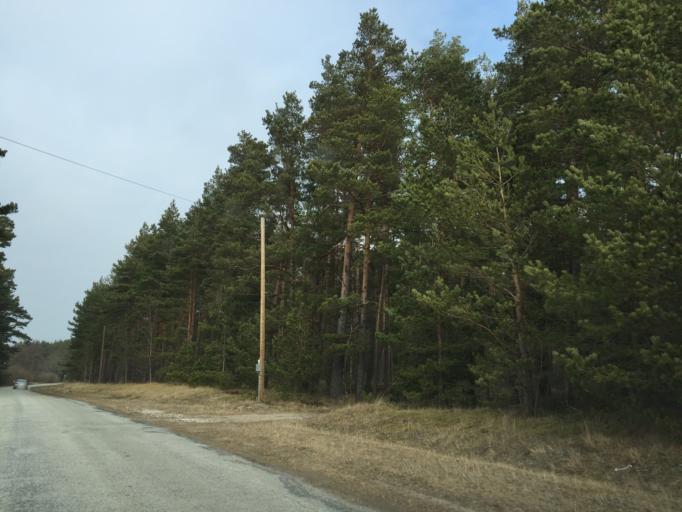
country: LV
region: Salacgrivas
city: Ainazi
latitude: 57.9335
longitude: 24.3920
